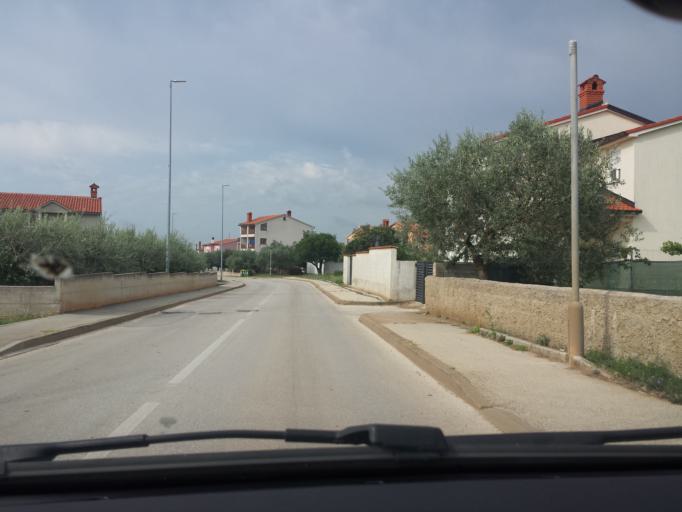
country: HR
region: Istarska
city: Galizana
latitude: 44.9289
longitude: 13.8674
